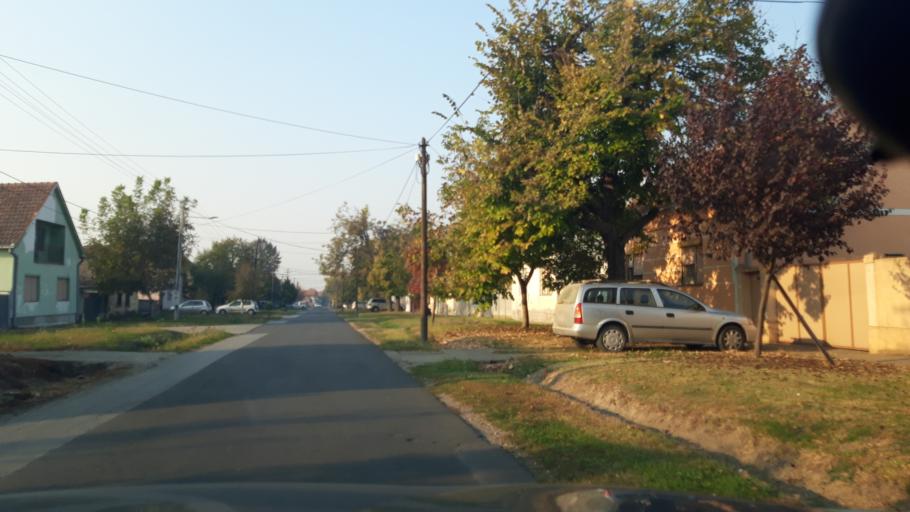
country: RS
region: Autonomna Pokrajina Vojvodina
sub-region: Sremski Okrug
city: Stara Pazova
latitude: 44.9929
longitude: 20.1472
